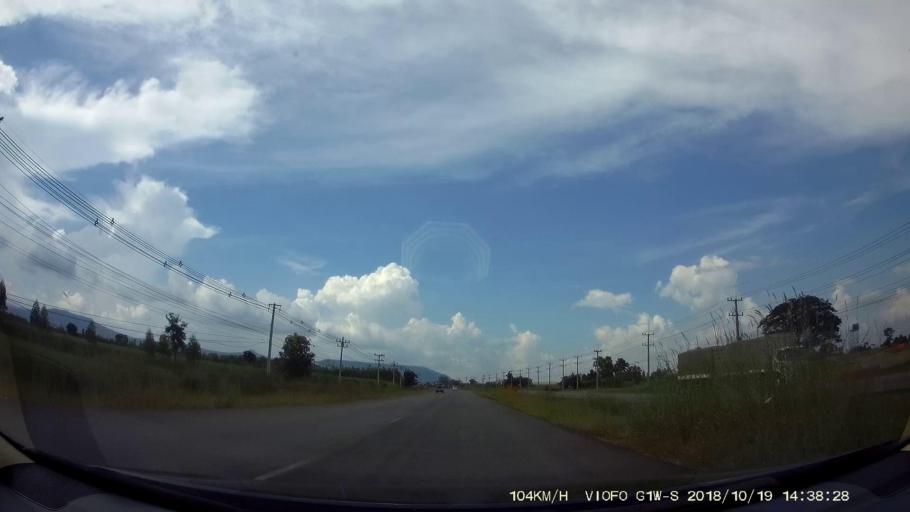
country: TH
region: Chaiyaphum
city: Kaeng Khro
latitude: 16.2134
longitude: 102.2017
